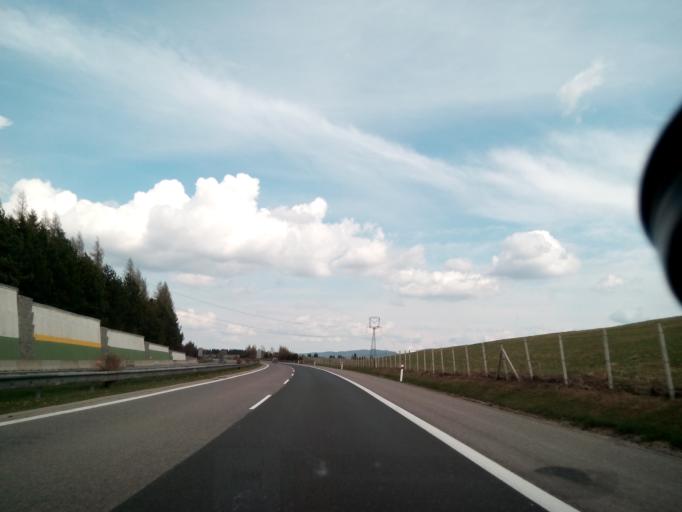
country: SK
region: Zilinsky
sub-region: Okres Liptovsky Mikulas
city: Hybe
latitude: 49.0510
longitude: 19.7836
